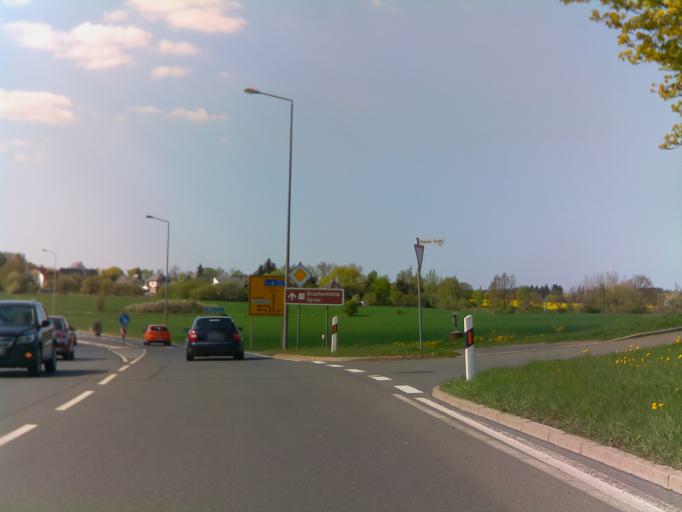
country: DE
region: Saxony
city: Syrau
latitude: 50.5325
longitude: 12.1070
